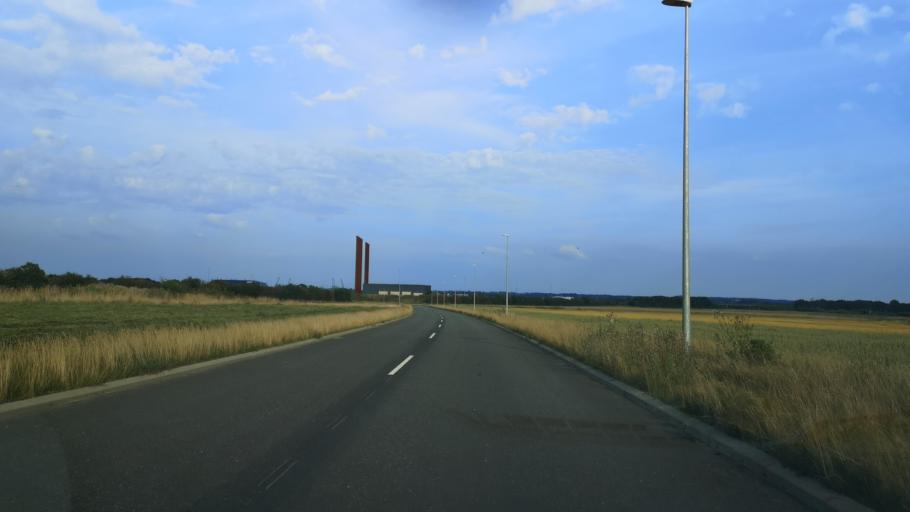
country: DK
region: Central Jutland
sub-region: Herning Kommune
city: Snejbjerg
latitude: 56.1179
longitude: 8.9228
